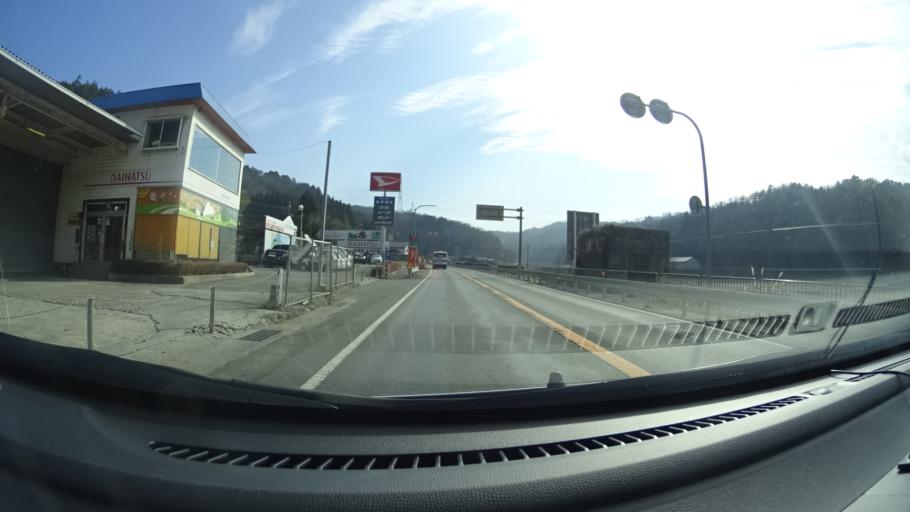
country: JP
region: Kyoto
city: Kameoka
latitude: 35.1323
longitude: 135.4303
